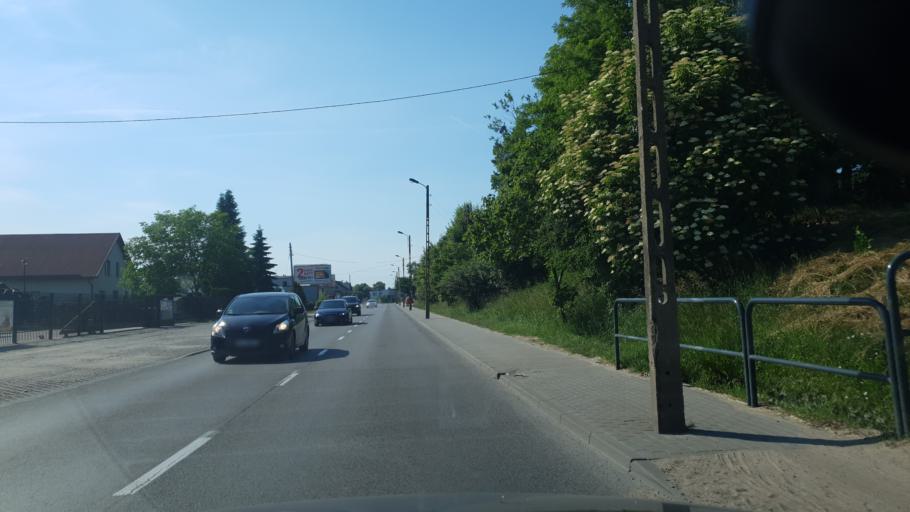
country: PL
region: Pomeranian Voivodeship
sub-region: Gdynia
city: Wielki Kack
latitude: 54.4387
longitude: 18.4606
